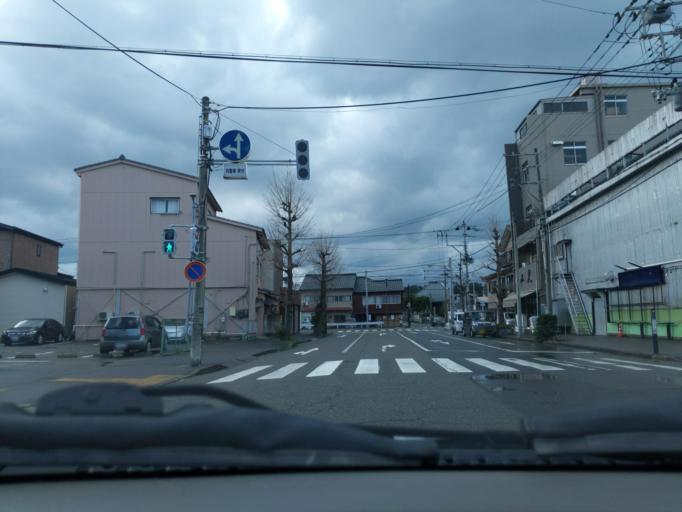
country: JP
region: Niigata
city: Niigata-shi
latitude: 37.9288
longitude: 139.0463
